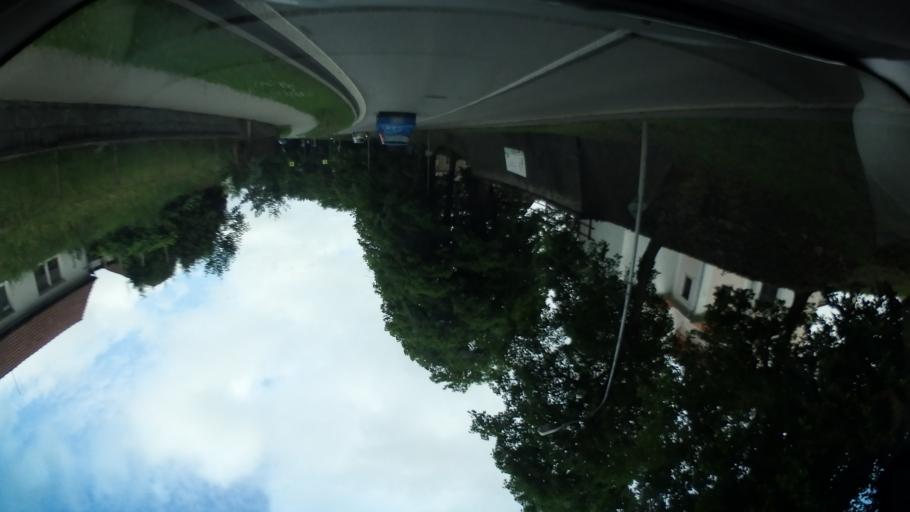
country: CZ
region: South Moravian
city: Kurim
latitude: 49.2969
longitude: 16.5265
